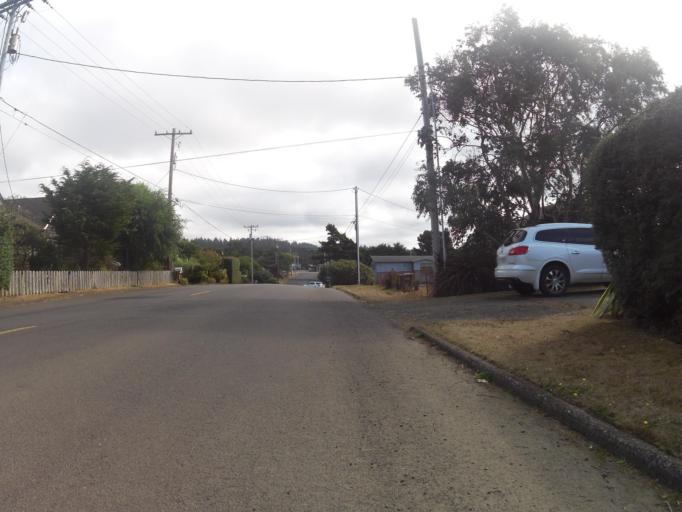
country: US
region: Oregon
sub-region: Lincoln County
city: Newport
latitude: 44.6482
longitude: -124.0567
